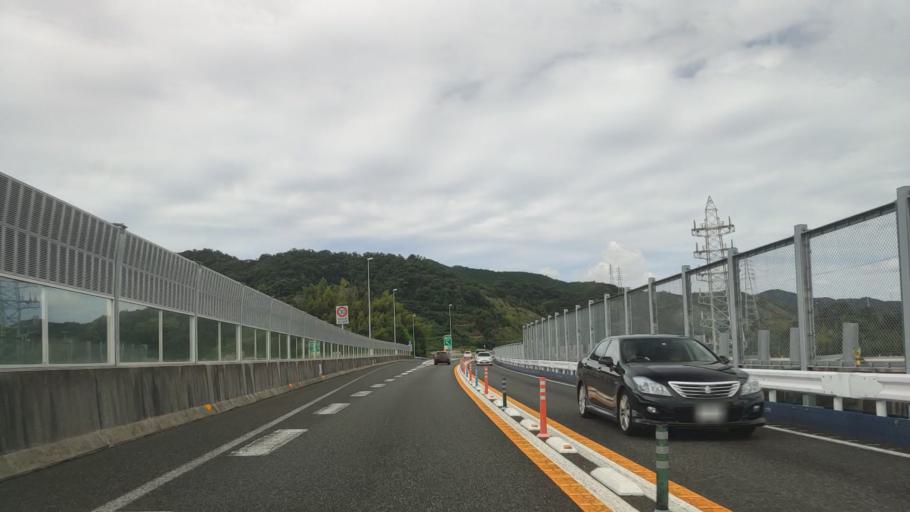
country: JP
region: Wakayama
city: Gobo
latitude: 33.8233
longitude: 135.2212
